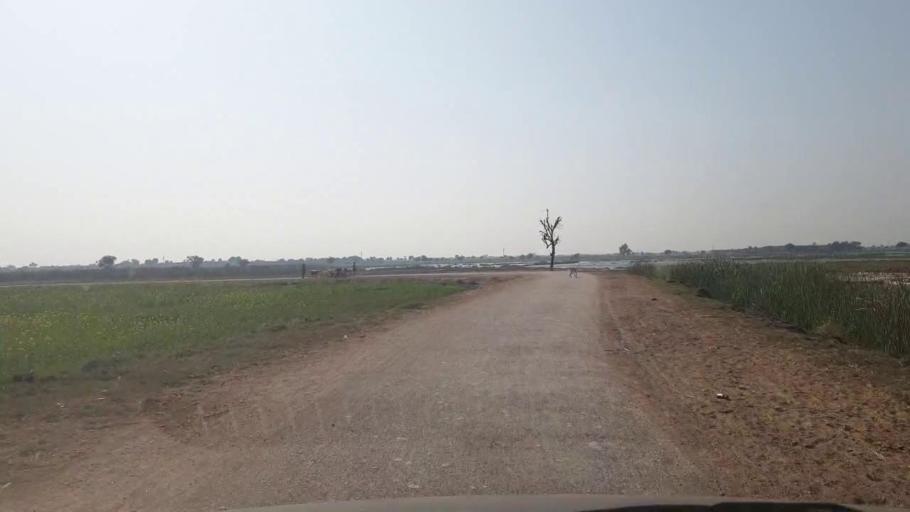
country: PK
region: Sindh
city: Tando Adam
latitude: 25.7470
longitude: 68.6138
